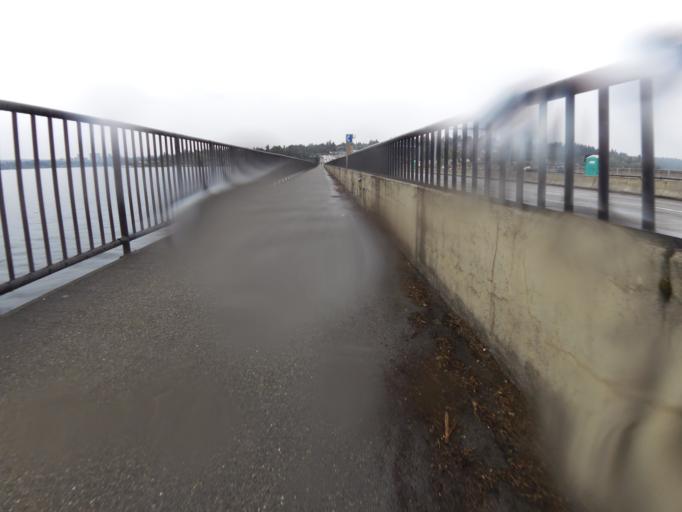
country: US
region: Washington
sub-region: King County
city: Mercer Island
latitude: 47.5903
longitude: -122.2625
